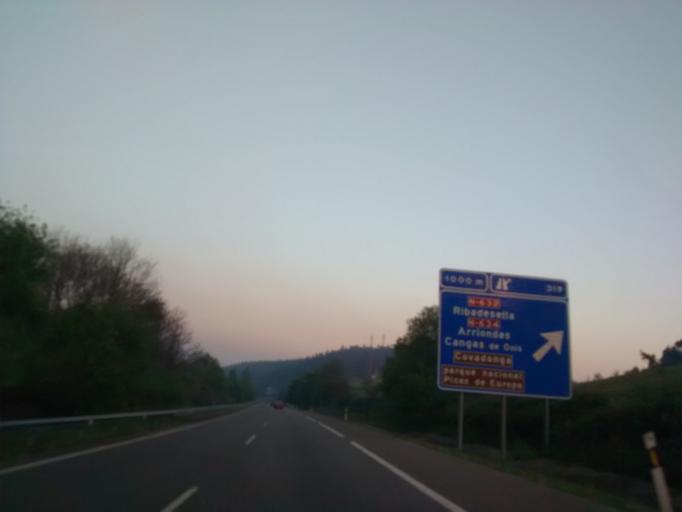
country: ES
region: Asturias
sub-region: Province of Asturias
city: Ribadesella
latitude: 43.4396
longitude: -5.0253
